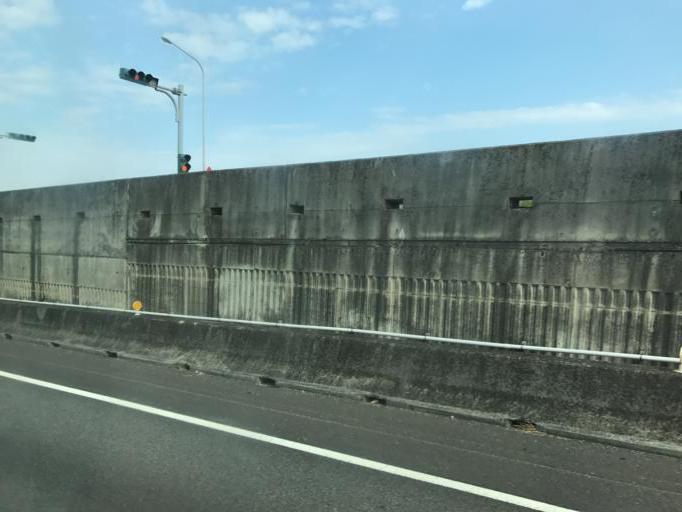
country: TW
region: Taiwan
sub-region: Hsinchu
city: Zhubei
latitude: 24.7996
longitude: 121.0089
